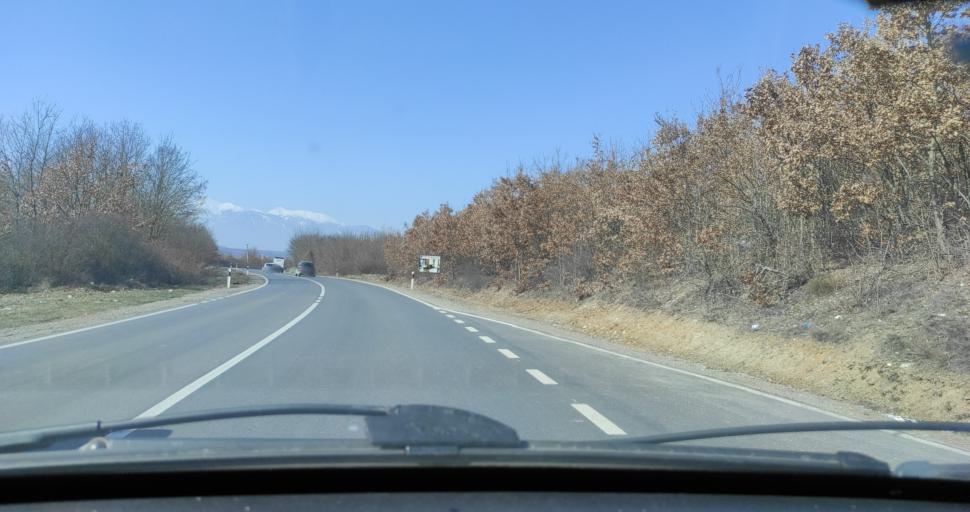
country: XK
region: Pec
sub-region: Komuna e Klines
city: Klina
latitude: 42.5958
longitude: 20.5381
